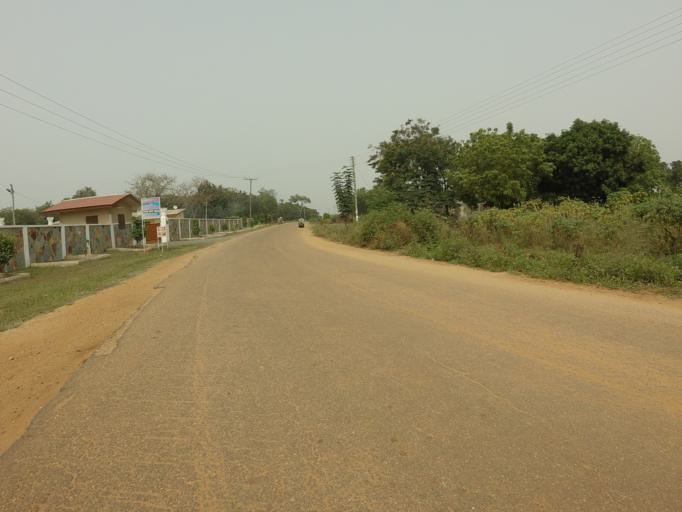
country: GH
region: Volta
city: Anloga
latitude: 5.9940
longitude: 0.5923
